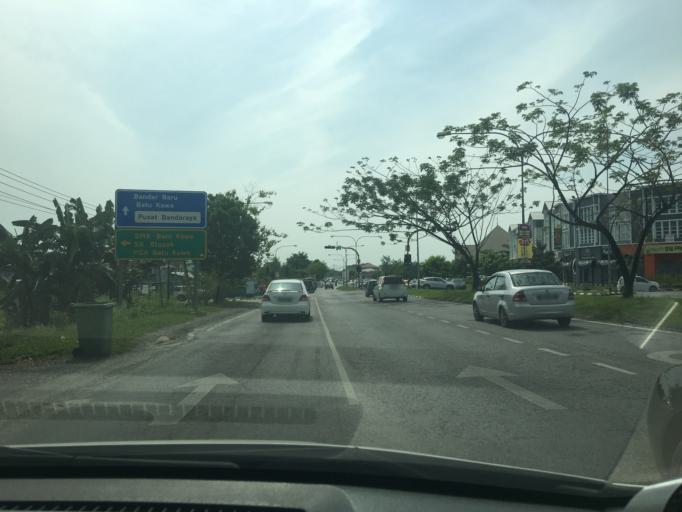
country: MY
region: Sarawak
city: Kuching
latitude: 1.5085
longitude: 110.2972
